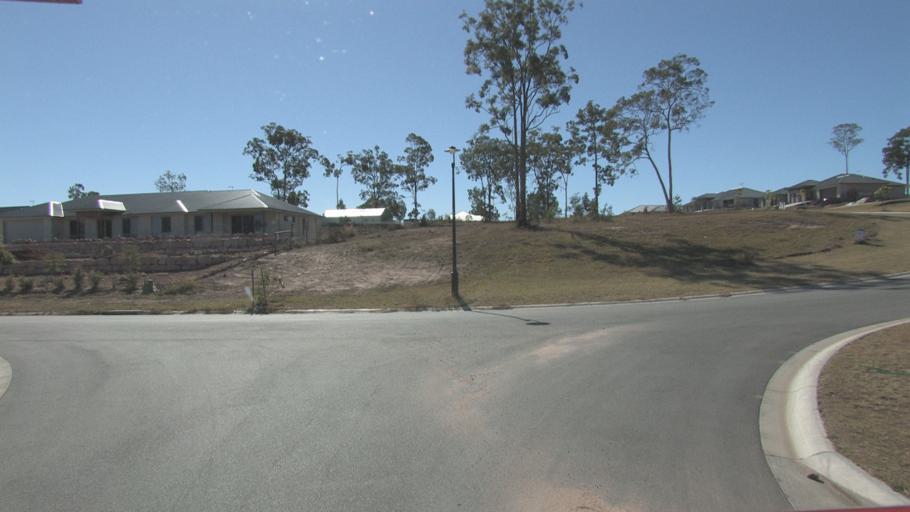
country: AU
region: Queensland
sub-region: Logan
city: North Maclean
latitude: -27.7504
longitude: 152.9443
